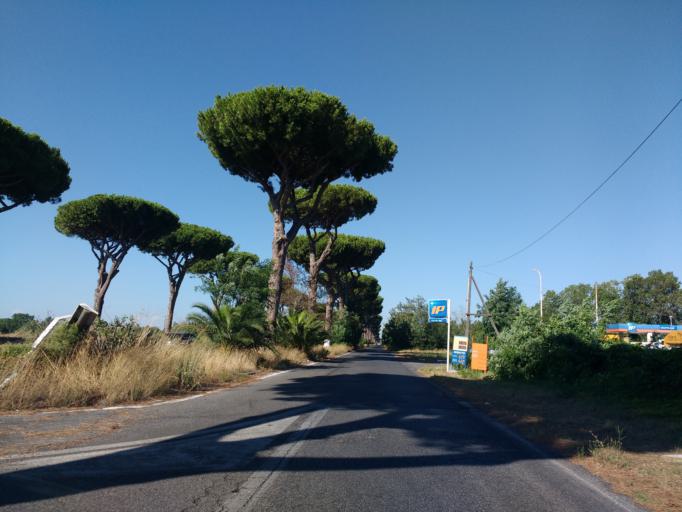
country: IT
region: Latium
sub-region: Citta metropolitana di Roma Capitale
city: Acilia-Castel Fusano-Ostia Antica
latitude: 41.7321
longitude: 12.3405
